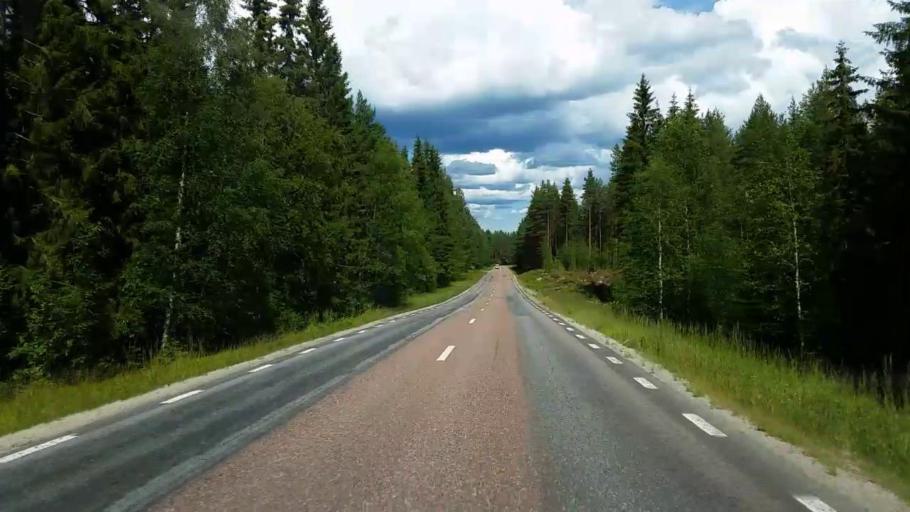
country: SE
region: Gaevleborg
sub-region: Ovanakers Kommun
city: Edsbyn
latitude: 61.3263
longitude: 15.5205
